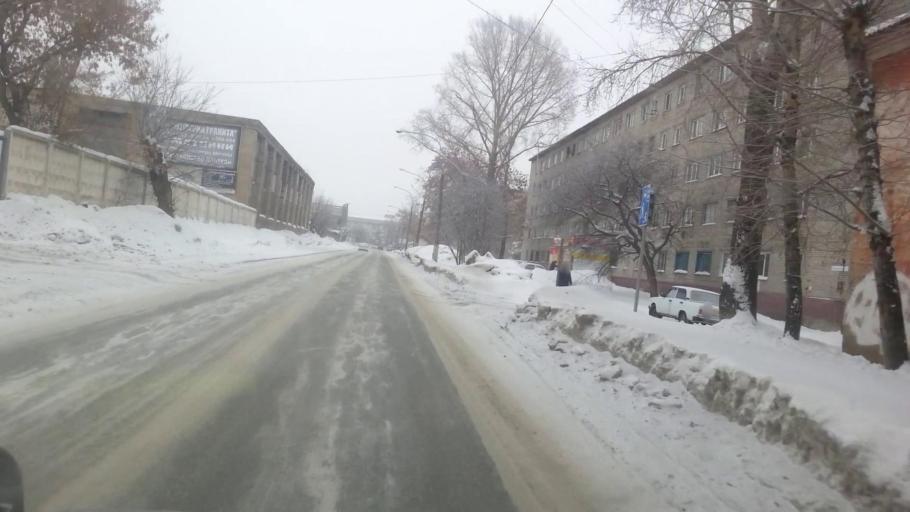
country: RU
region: Altai Krai
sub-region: Gorod Barnaulskiy
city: Barnaul
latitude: 53.3815
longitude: 83.7349
